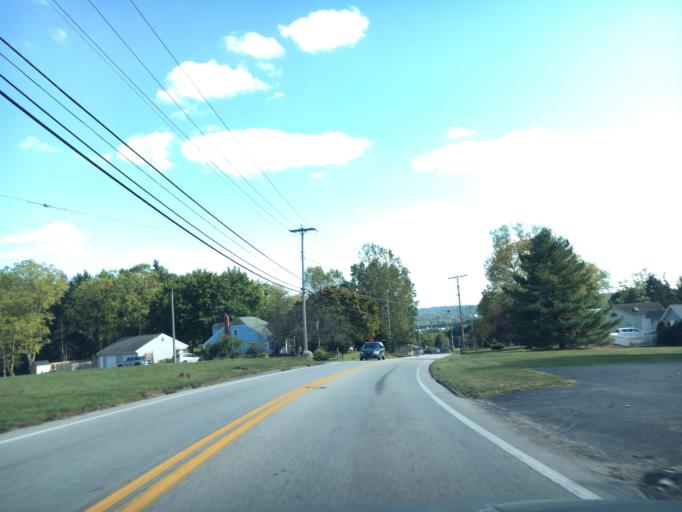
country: US
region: Pennsylvania
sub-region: York County
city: East York
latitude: 39.9986
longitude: -76.6781
